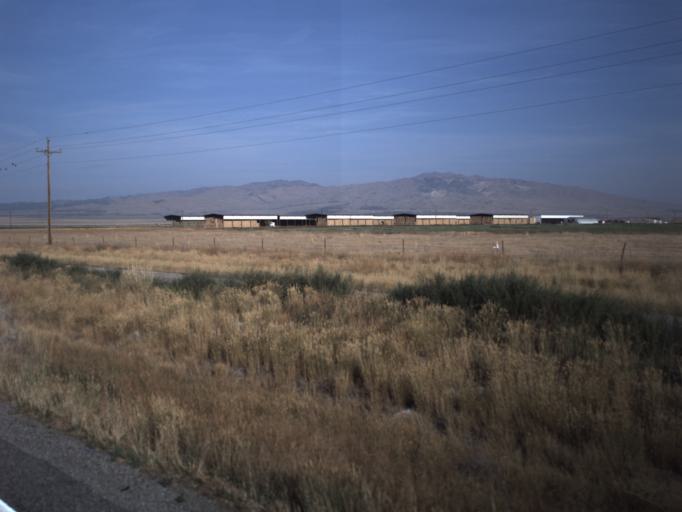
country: US
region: Idaho
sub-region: Oneida County
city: Malad City
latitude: 41.9667
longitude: -112.8969
